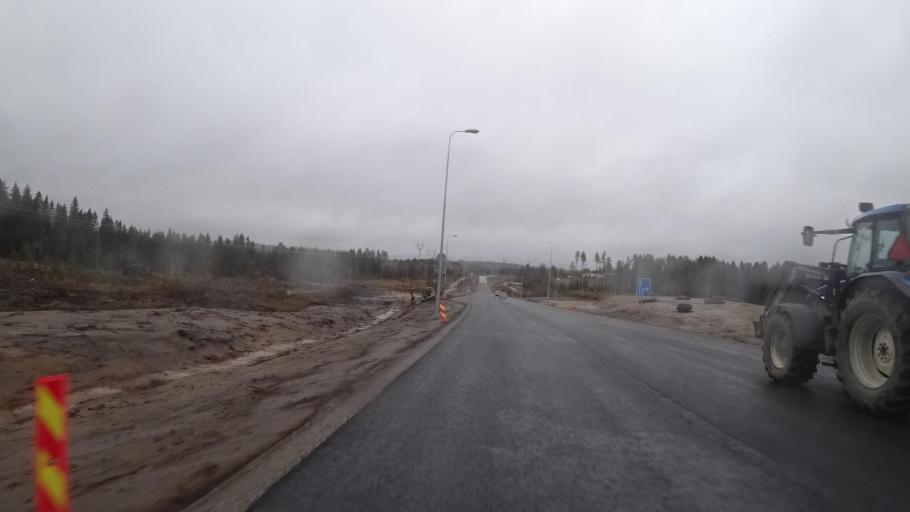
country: FI
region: Northern Savo
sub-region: Varkaus
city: Kangaslampi
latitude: 62.3970
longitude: 28.1527
